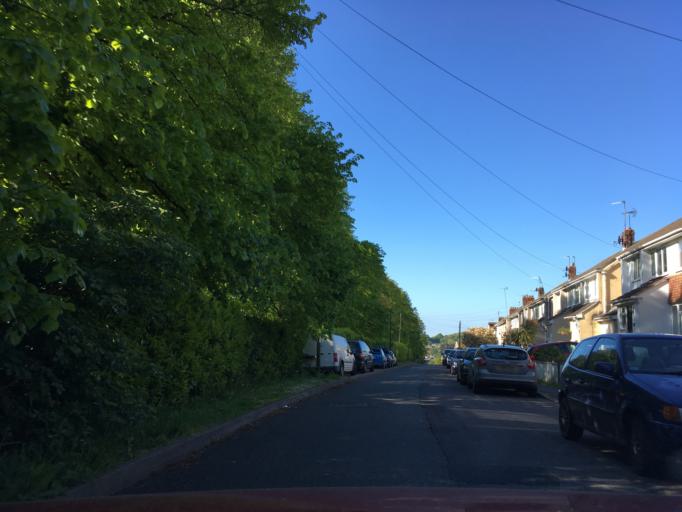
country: GB
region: England
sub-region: North Somerset
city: Portishead
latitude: 51.4919
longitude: -2.7638
